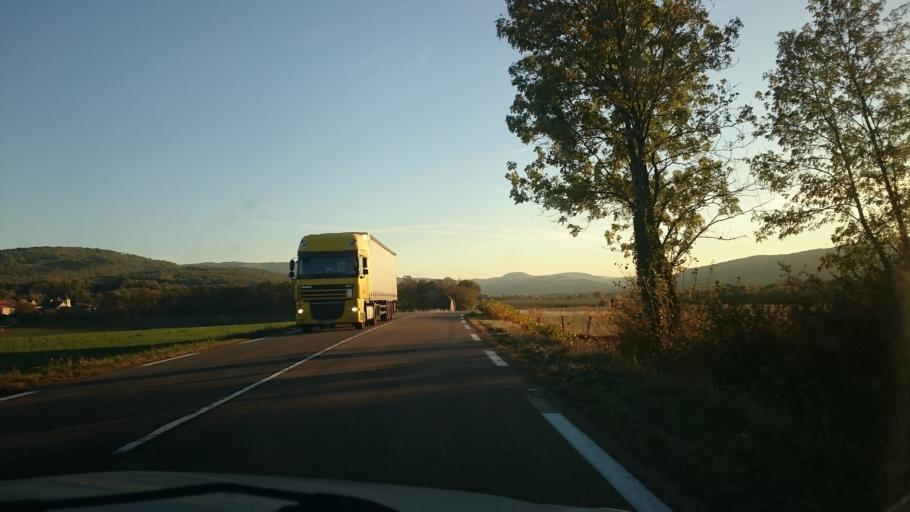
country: FR
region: Franche-Comte
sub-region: Departement du Doubs
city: Quingey
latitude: 47.0505
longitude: 5.8783
